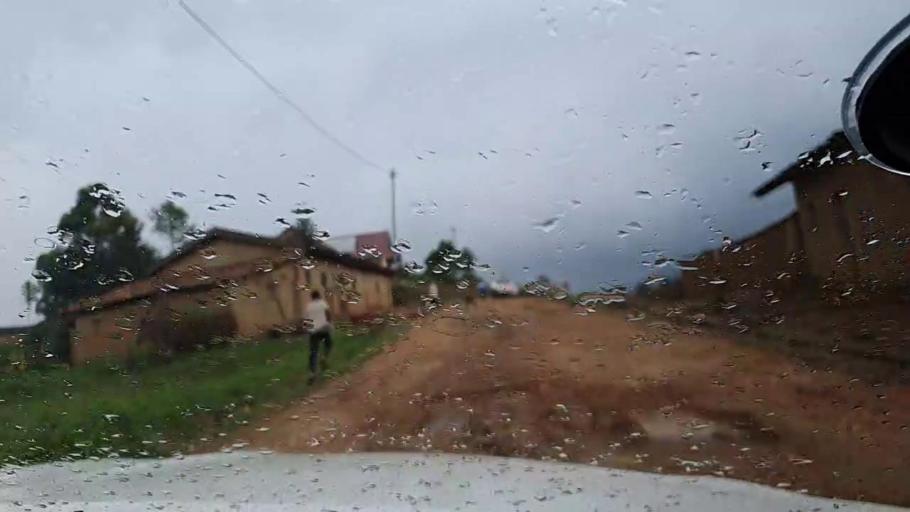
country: RW
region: Western Province
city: Kibuye
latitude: -2.1097
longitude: 29.4839
